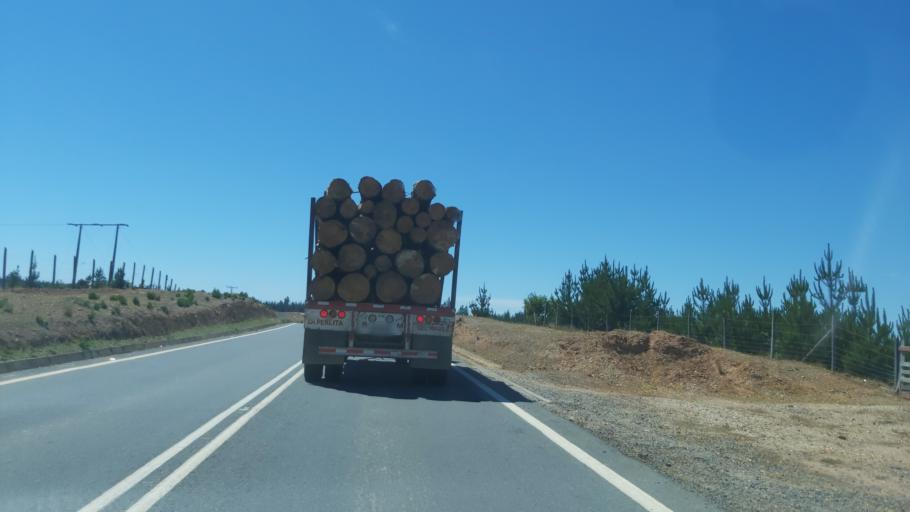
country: CL
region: Maule
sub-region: Provincia de Talca
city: Talca
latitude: -34.9456
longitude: -71.9747
